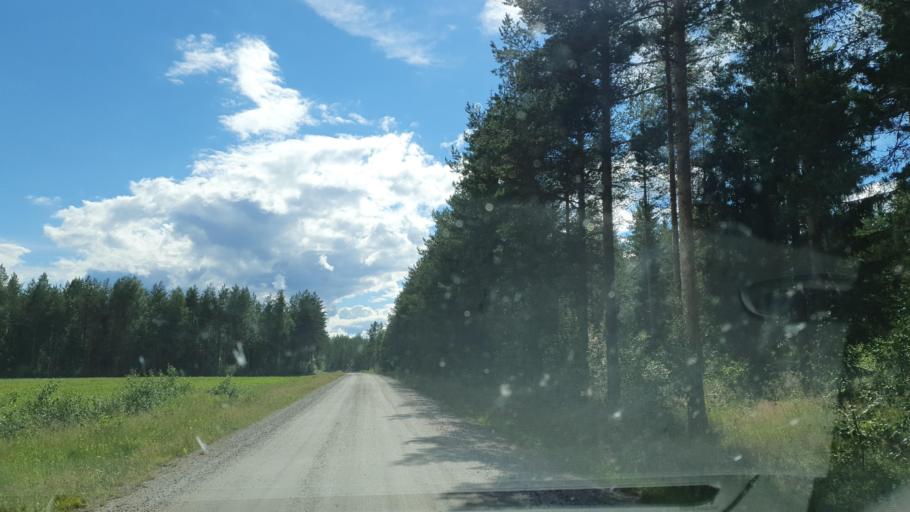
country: FI
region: Kainuu
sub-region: Kehys-Kainuu
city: Kuhmo
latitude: 64.1527
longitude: 29.7938
